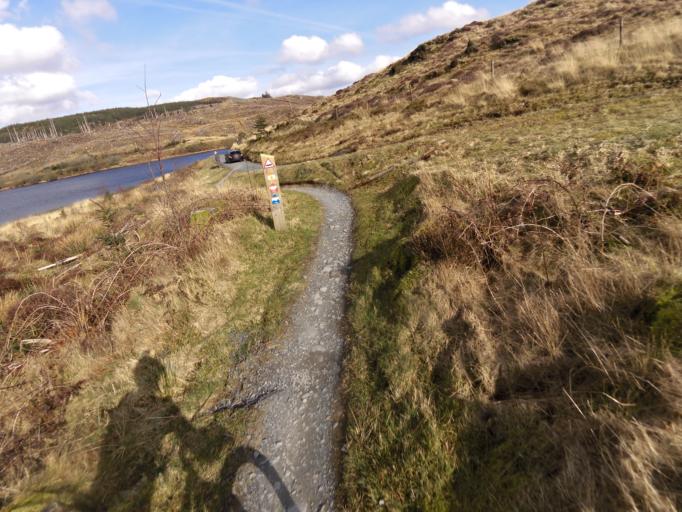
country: GB
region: Wales
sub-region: County of Ceredigion
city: Bow Street
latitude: 52.4337
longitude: -3.8924
